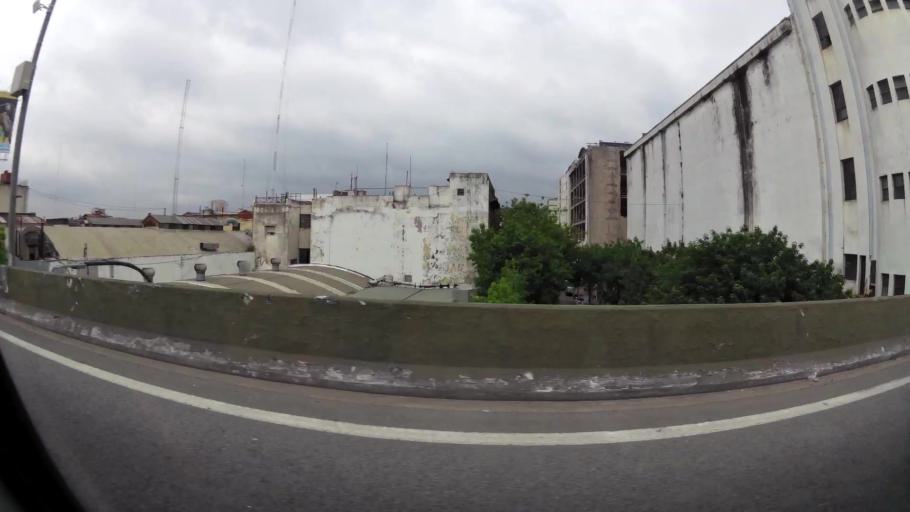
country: AR
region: Buenos Aires F.D.
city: Buenos Aires
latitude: -34.6276
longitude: -58.3586
